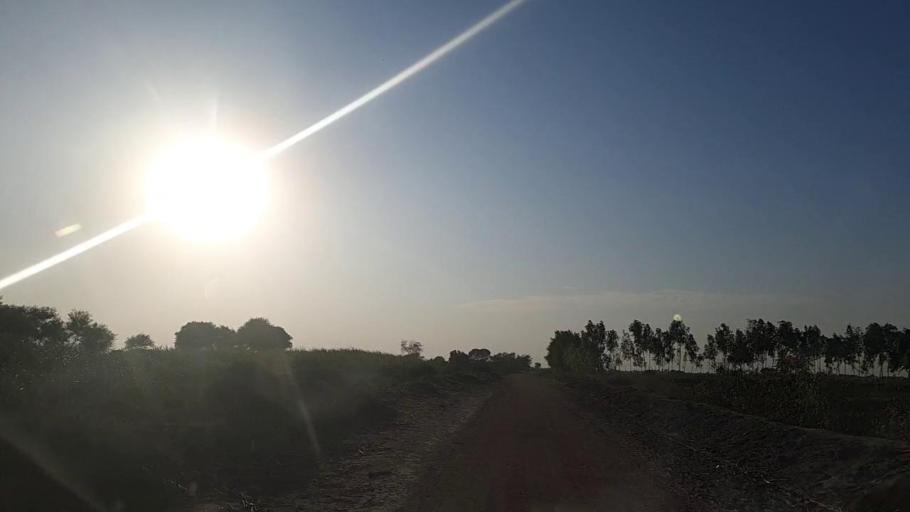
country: PK
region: Sindh
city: Jati
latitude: 24.4176
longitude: 68.1722
